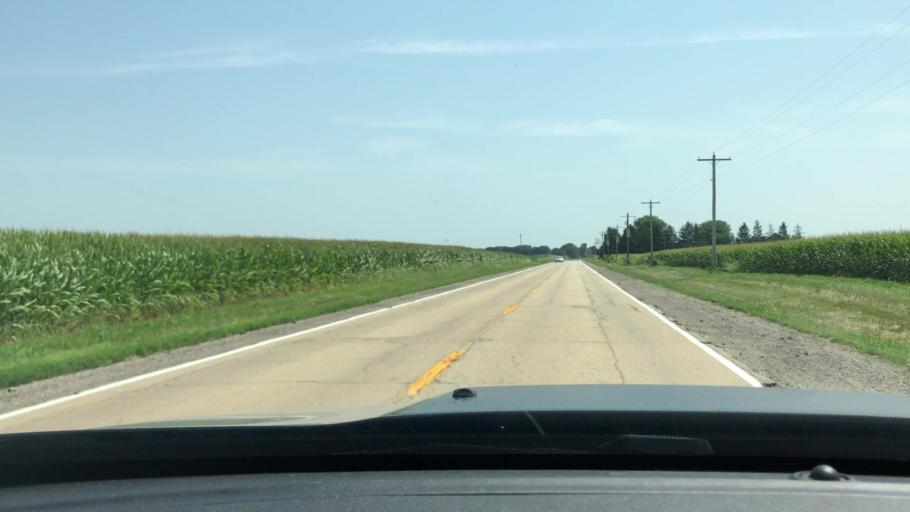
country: US
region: Illinois
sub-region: LaSalle County
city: Sheridan
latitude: 41.4853
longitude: -88.7899
